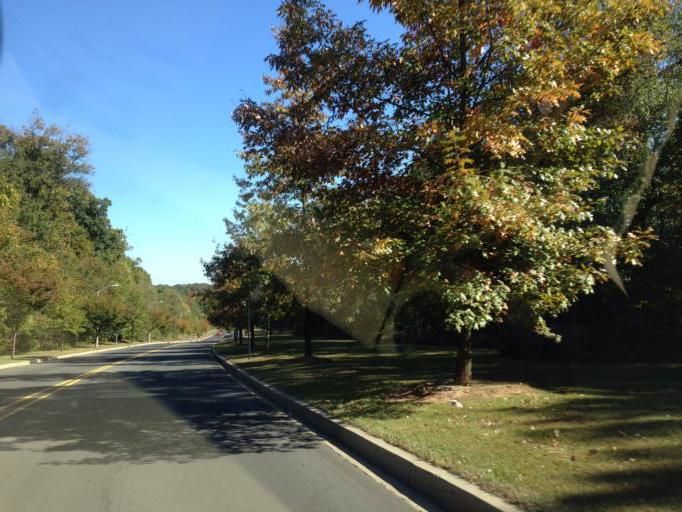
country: US
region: Maryland
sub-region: Montgomery County
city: Germantown
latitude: 39.1928
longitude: -77.2379
